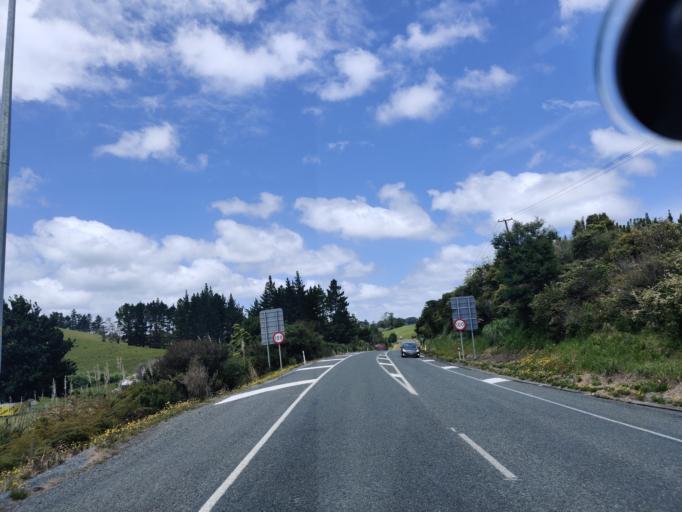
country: NZ
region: Auckland
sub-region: Auckland
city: Wellsford
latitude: -36.2584
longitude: 174.5098
